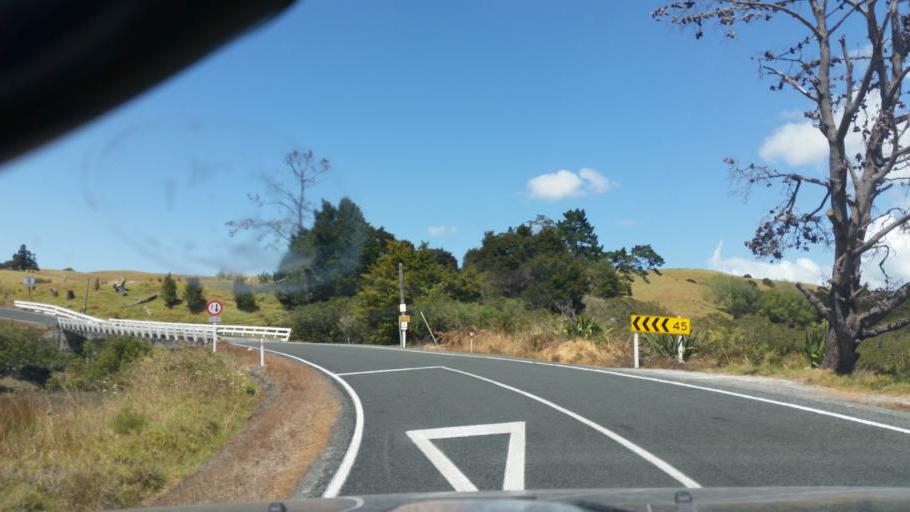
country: NZ
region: Northland
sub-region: Whangarei
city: Ruakaka
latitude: -36.1144
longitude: 174.2289
